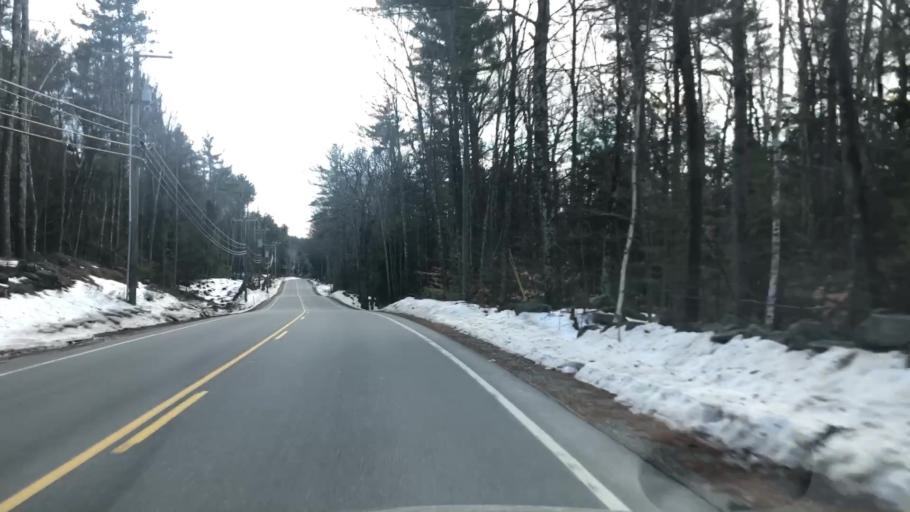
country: US
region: New Hampshire
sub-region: Hillsborough County
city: Mont Vernon
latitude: 42.8788
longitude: -71.6697
